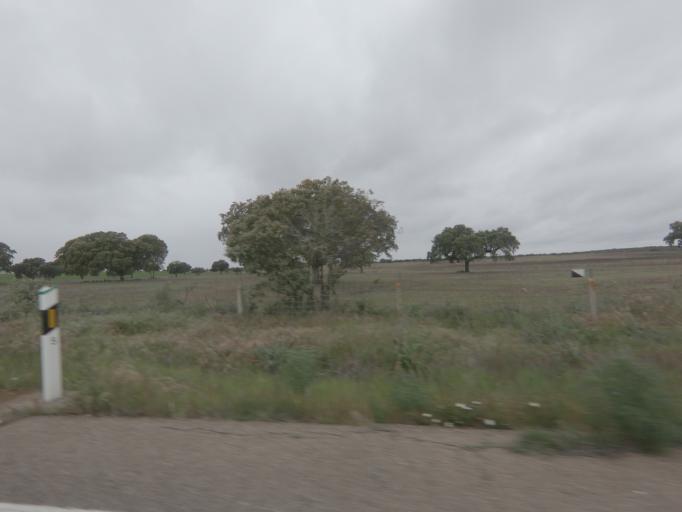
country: ES
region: Extremadura
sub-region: Provincia de Badajoz
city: Badajoz
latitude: 38.9656
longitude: -6.8982
